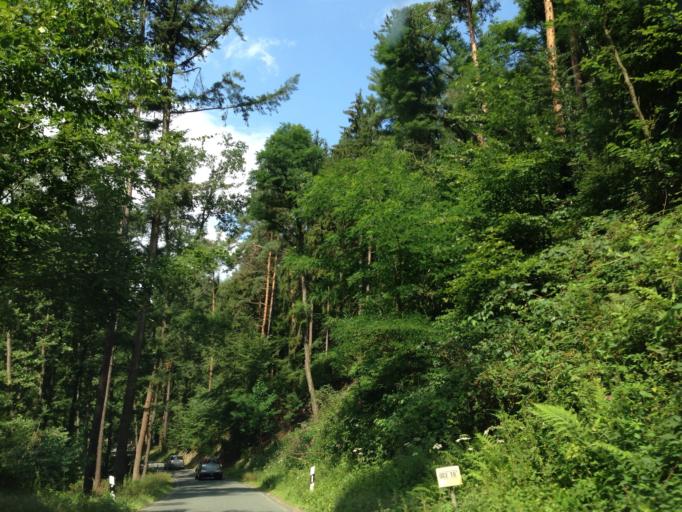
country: DE
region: Thuringia
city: Herschdorf
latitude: 50.7419
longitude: 11.5260
